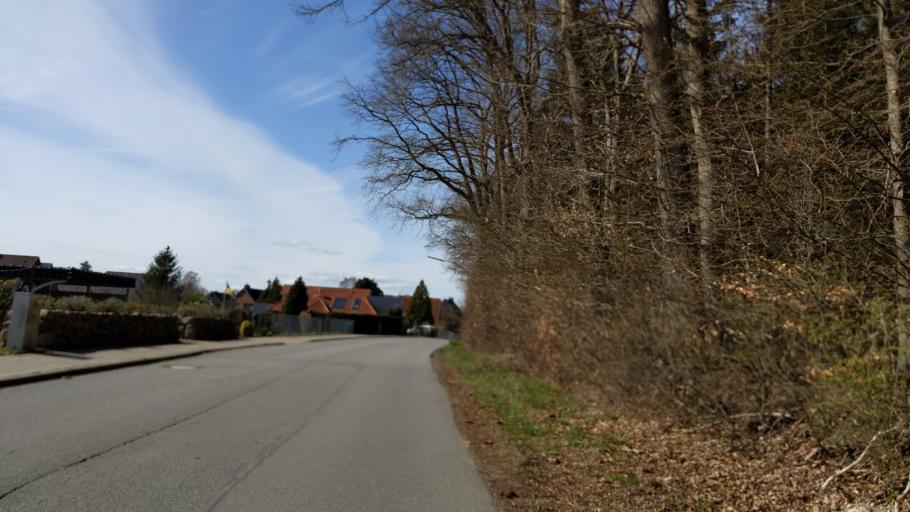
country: DE
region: Schleswig-Holstein
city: Ratekau
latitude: 53.9663
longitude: 10.7082
